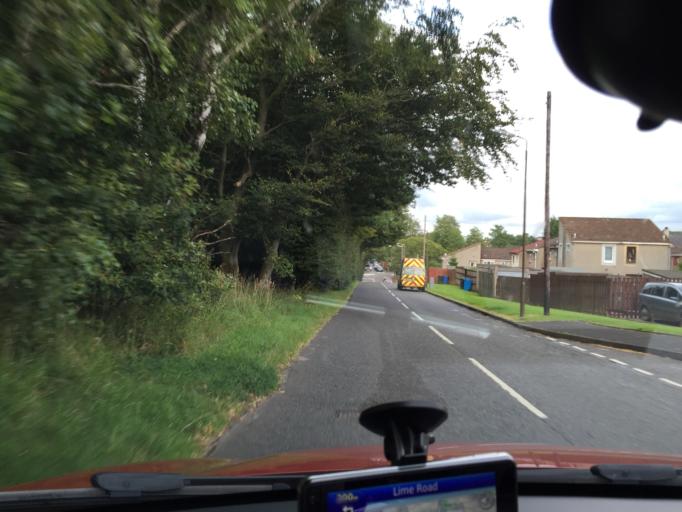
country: GB
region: Scotland
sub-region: Falkirk
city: Larbert
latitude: 55.9975
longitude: -3.8366
